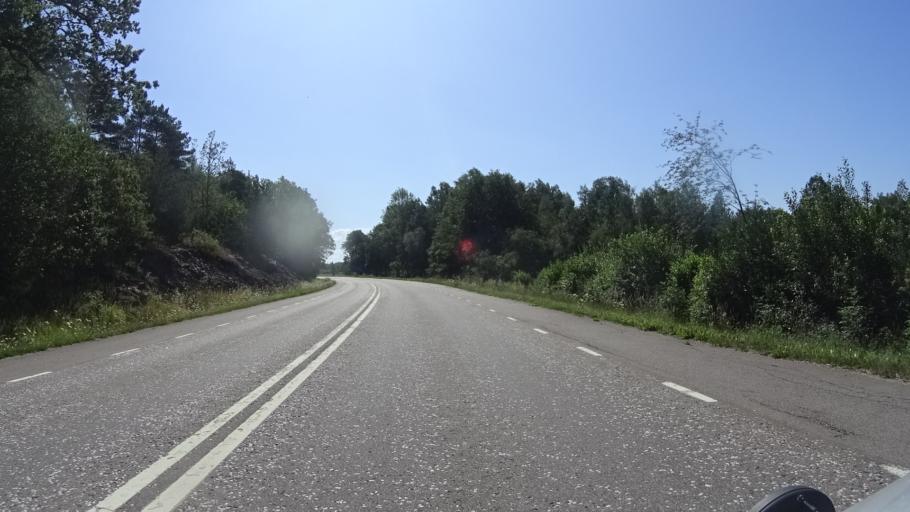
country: SE
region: OEstergoetland
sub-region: Vadstena Kommun
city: Herrestad
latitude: 58.3063
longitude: 14.9138
